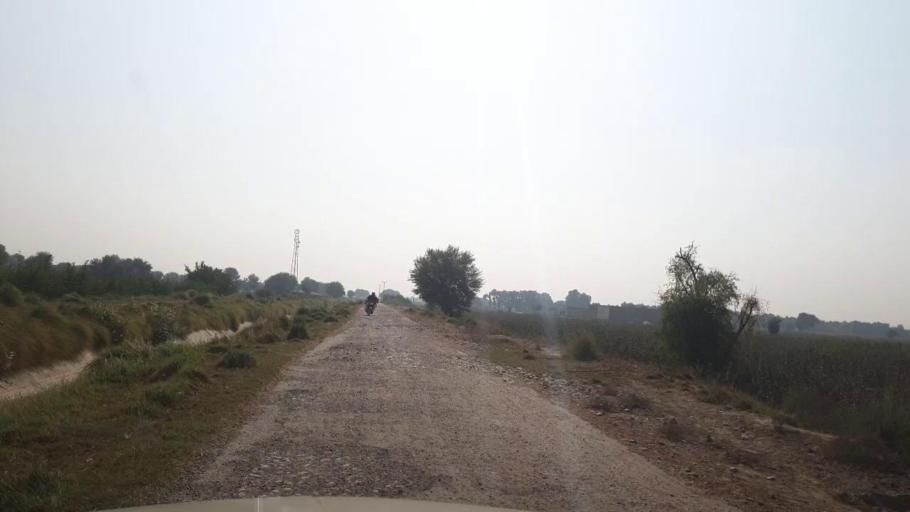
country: PK
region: Sindh
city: Bhan
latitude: 26.5317
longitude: 67.7774
